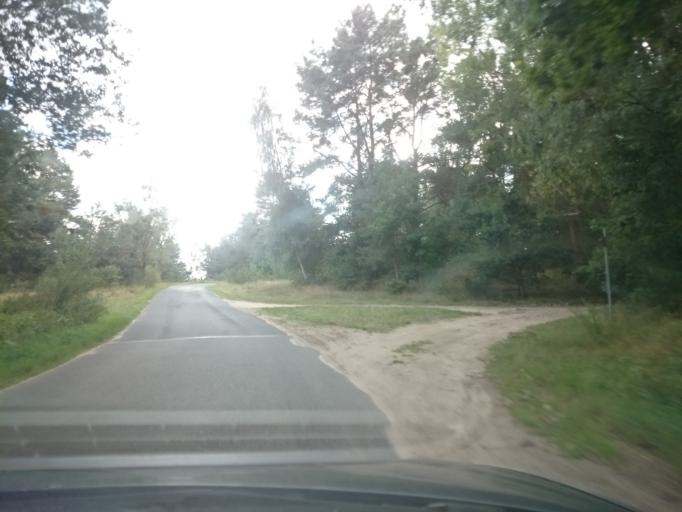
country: DE
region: Mecklenburg-Vorpommern
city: Carpin
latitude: 53.3643
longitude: 13.2499
